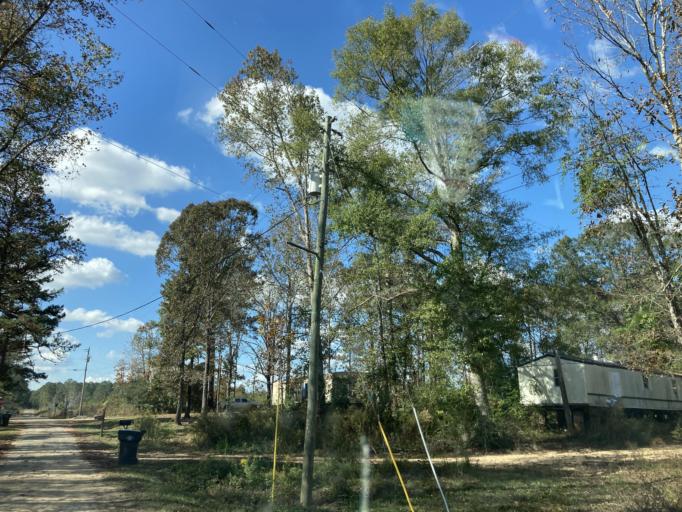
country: US
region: Mississippi
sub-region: Lamar County
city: Sumrall
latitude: 31.3527
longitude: -89.5433
